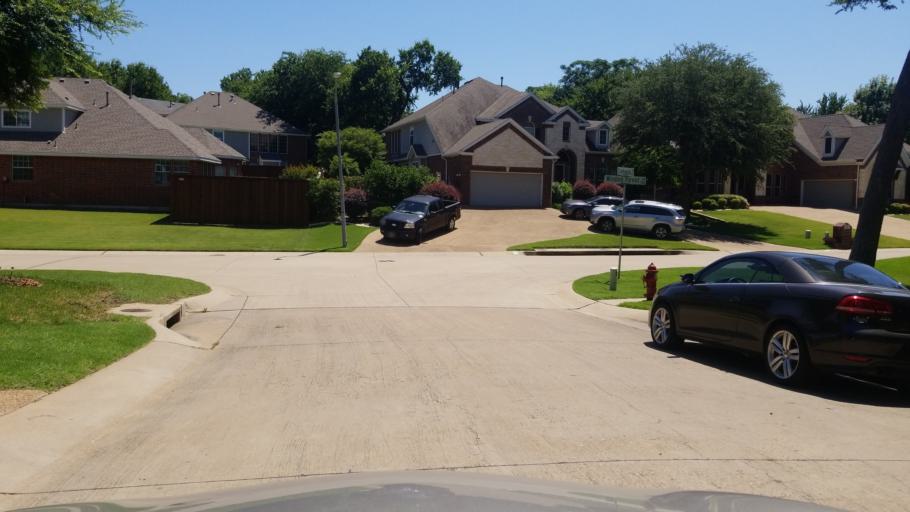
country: US
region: Texas
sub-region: Dallas County
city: Grand Prairie
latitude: 32.6836
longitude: -97.0010
